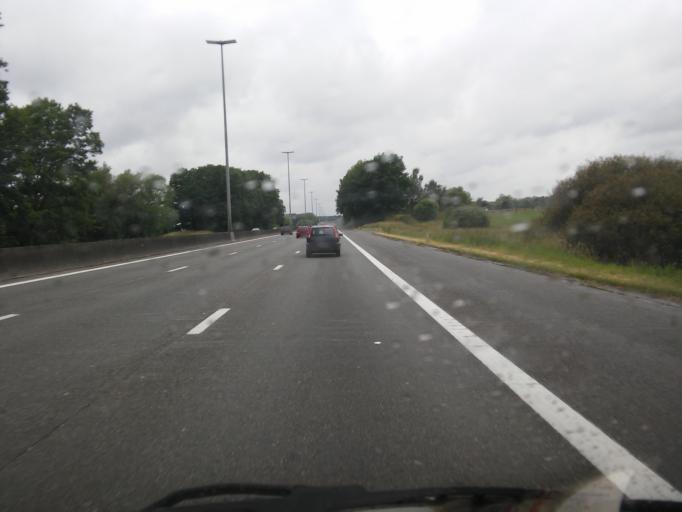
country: BE
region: Flanders
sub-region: Provincie Vlaams-Brabant
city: Ternat
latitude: 50.8868
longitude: 4.1415
